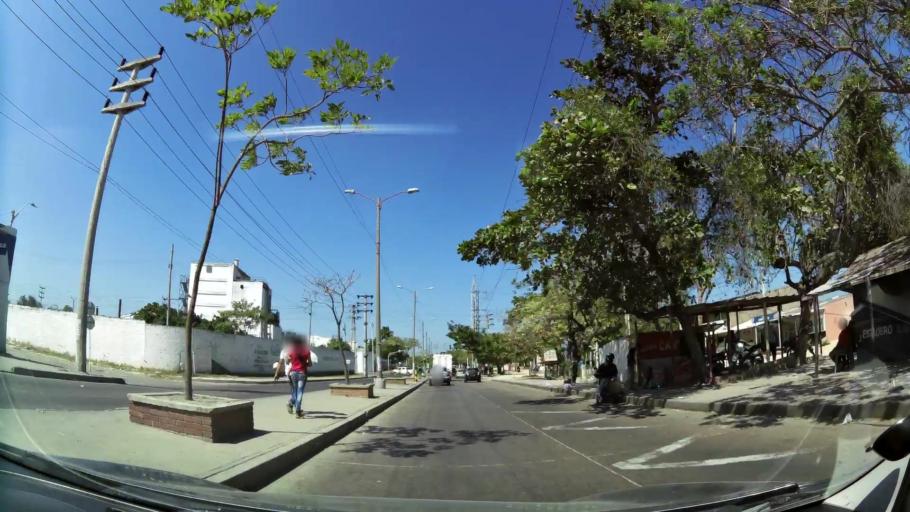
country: CO
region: Atlantico
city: Barranquilla
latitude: 10.9531
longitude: -74.7739
